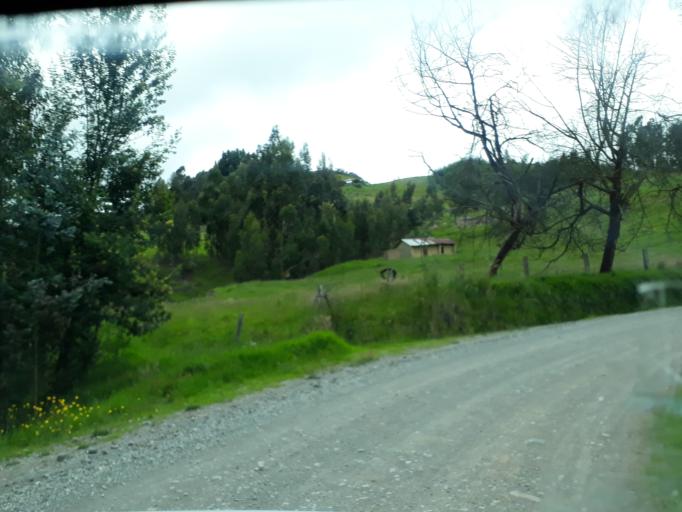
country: CO
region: Cundinamarca
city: La Mesa
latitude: 5.2881
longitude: -73.9027
